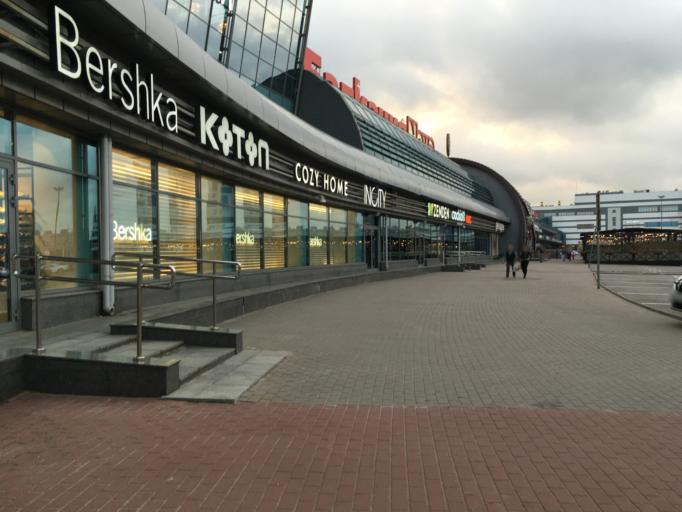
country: RU
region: St.-Petersburg
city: Shushary
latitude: 59.8261
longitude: 30.3809
